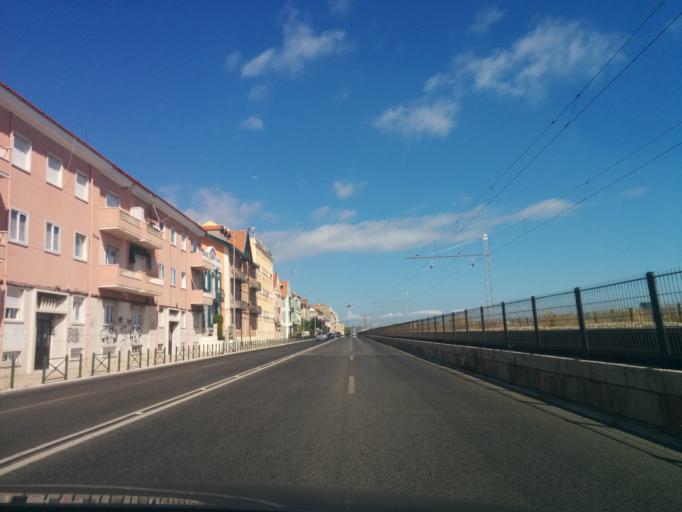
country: PT
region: Lisbon
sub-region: Oeiras
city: Linda-a-Velha
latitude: 38.6995
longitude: -9.2461
